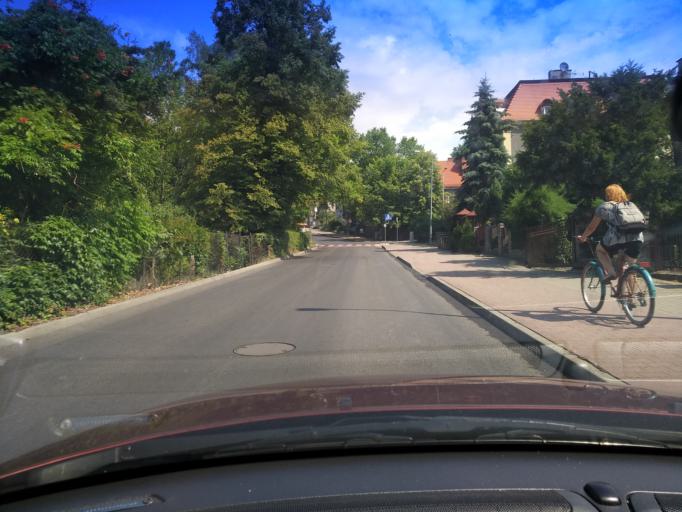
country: PL
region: Lower Silesian Voivodeship
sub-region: Powiat zgorzelecki
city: Zgorzelec
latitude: 51.1362
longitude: 15.0063
